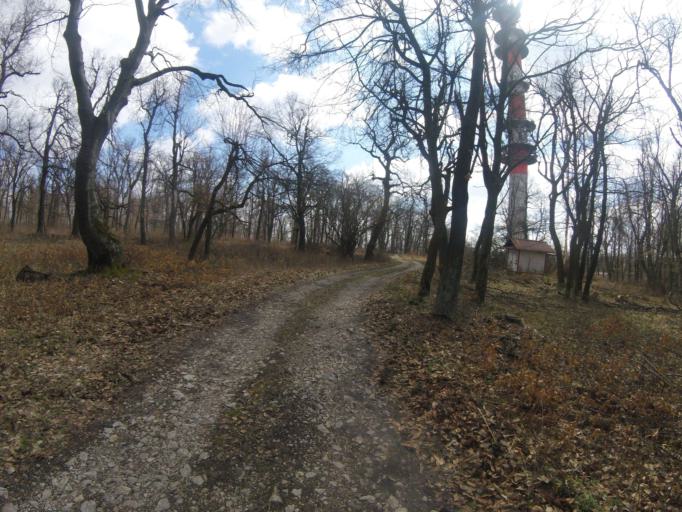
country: HU
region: Komarom-Esztergom
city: Tardos
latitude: 47.6772
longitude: 18.4935
